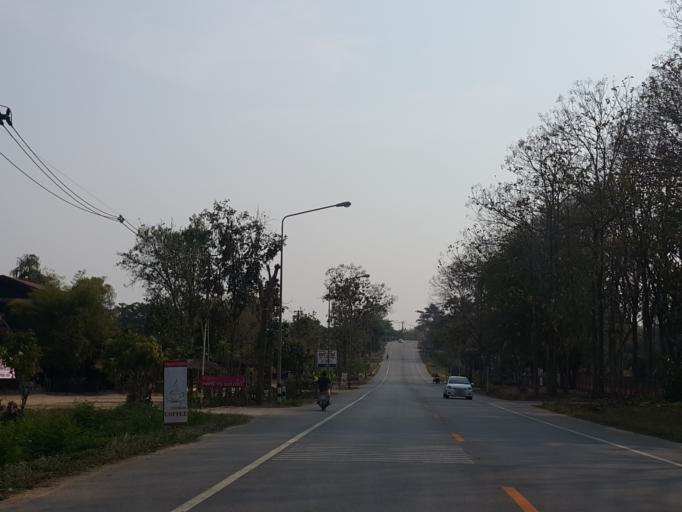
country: TH
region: Lampang
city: Chae Hom
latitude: 18.7188
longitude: 99.5614
